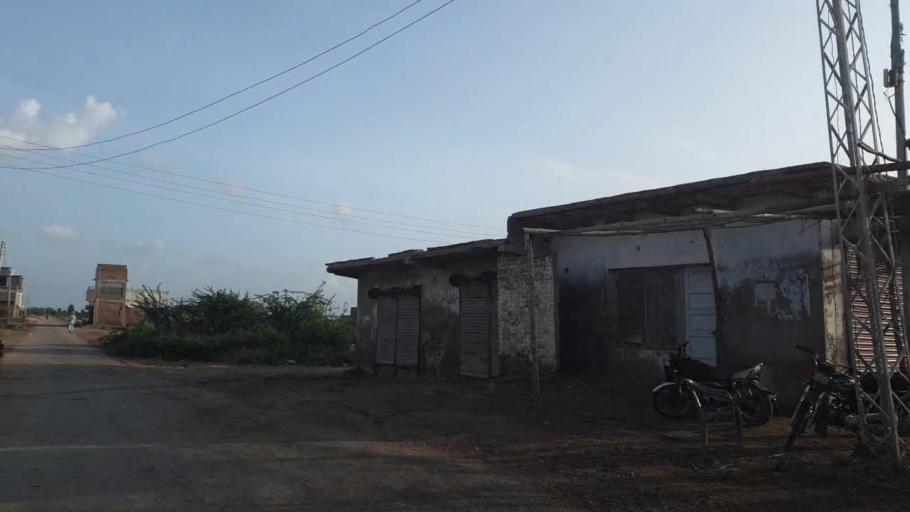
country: PK
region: Sindh
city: Kadhan
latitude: 24.6395
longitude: 69.1228
